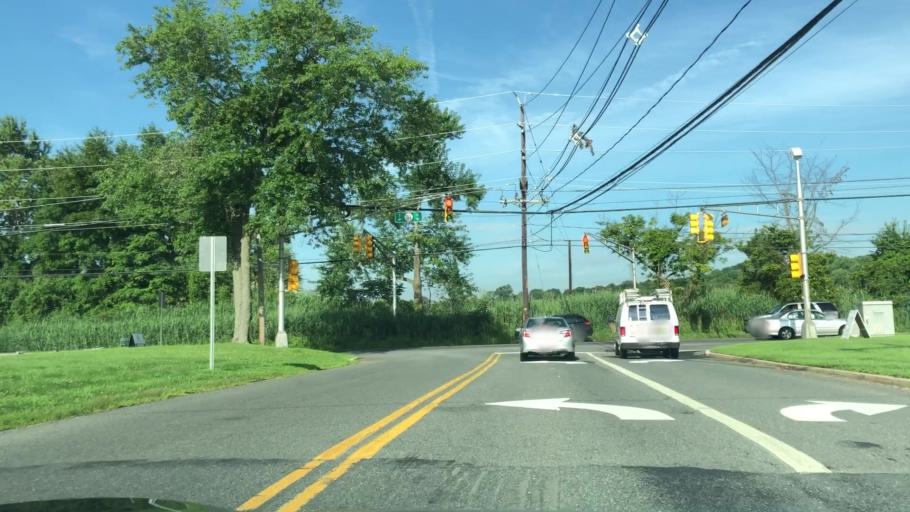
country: US
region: New Jersey
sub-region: Mercer County
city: Pennington
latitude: 40.3488
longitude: -74.7965
